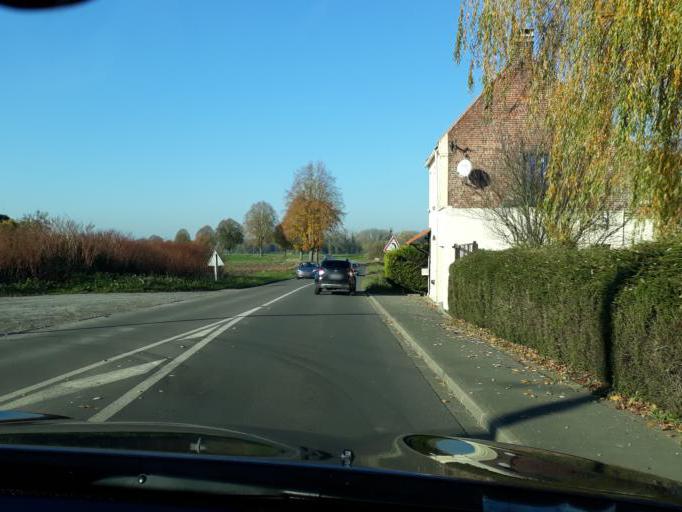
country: FR
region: Nord-Pas-de-Calais
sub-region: Departement du Nord
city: Guesnain
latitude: 50.3604
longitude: 3.1587
